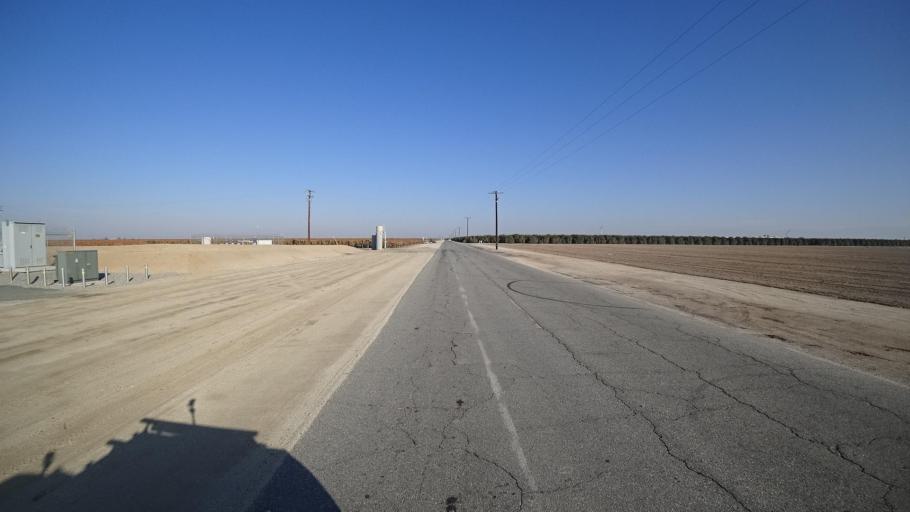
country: US
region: California
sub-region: Tulare County
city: Richgrove
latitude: 35.7819
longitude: -119.1697
